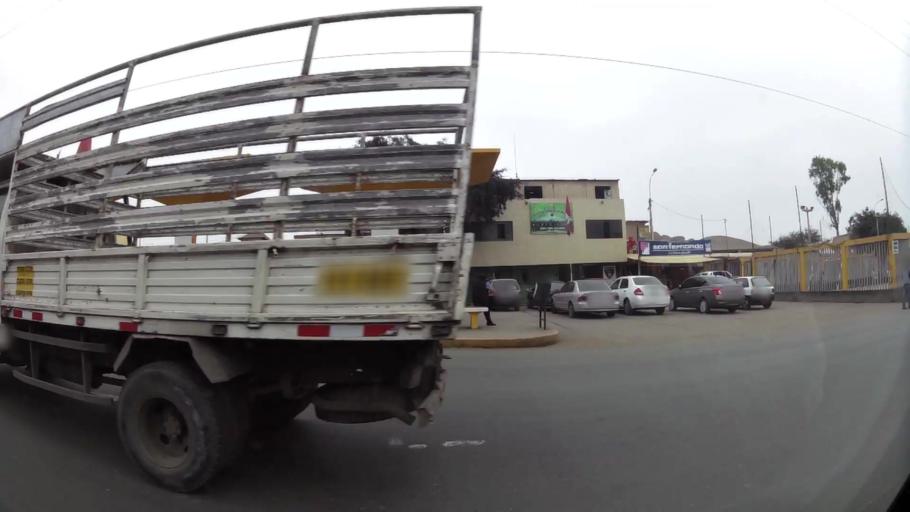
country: PE
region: Lima
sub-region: Lima
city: Punta Hermosa
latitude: -12.2528
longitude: -76.8983
